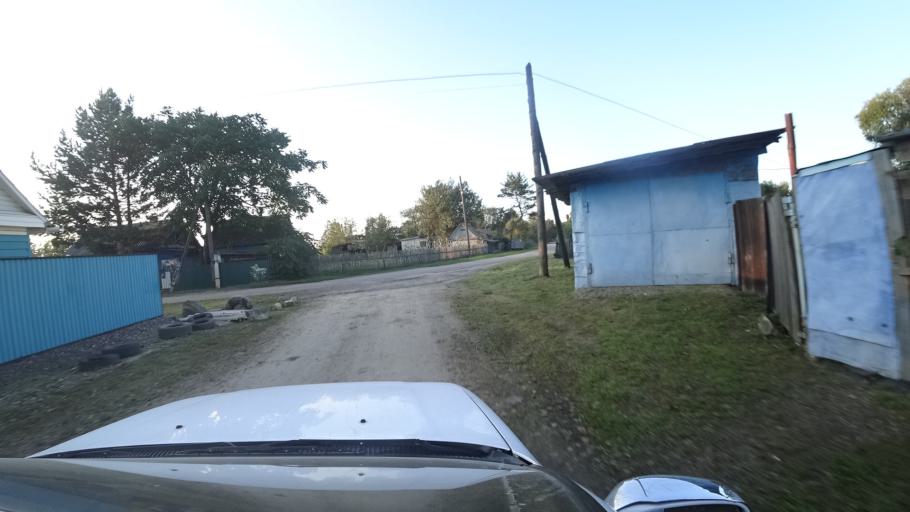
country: RU
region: Primorskiy
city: Dal'nerechensk
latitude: 45.9430
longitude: 133.7573
